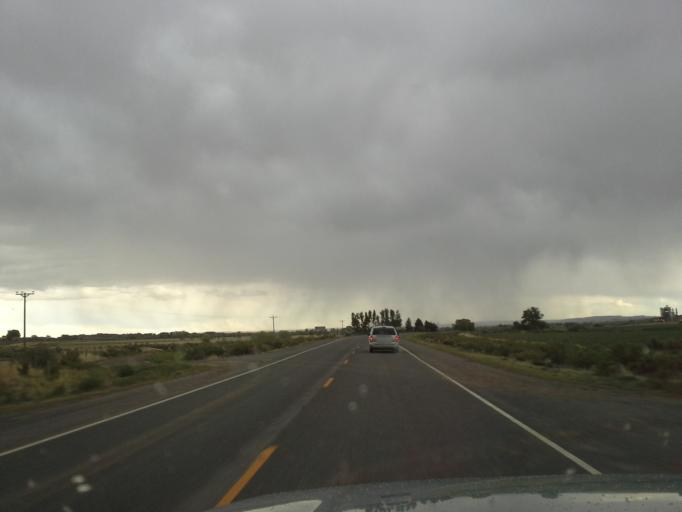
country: US
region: Wyoming
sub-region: Park County
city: Powell
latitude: 45.0076
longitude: -108.6240
